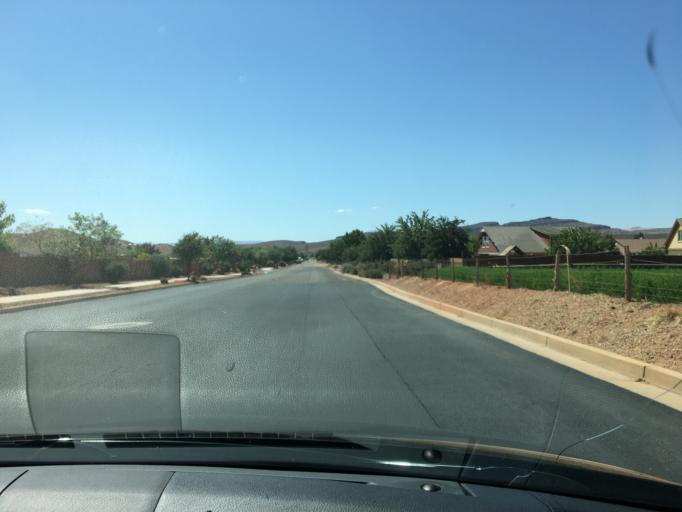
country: US
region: Utah
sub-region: Washington County
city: Ivins
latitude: 37.1662
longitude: -113.6888
